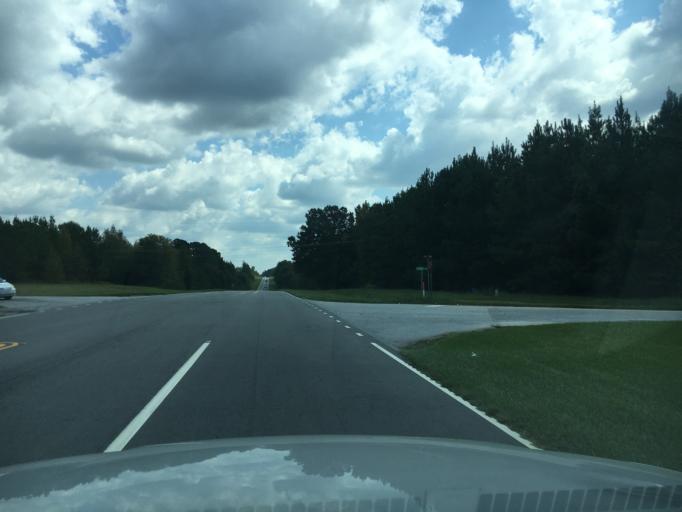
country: US
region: South Carolina
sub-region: Greenwood County
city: Greenwood
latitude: 34.1499
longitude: -82.1583
